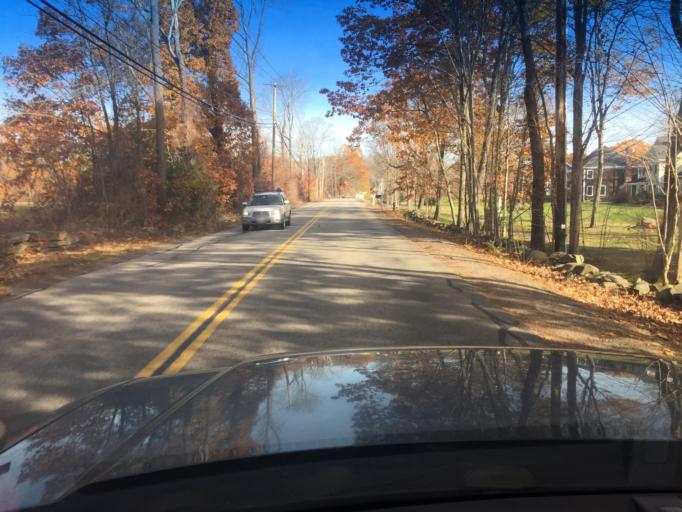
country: US
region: Maine
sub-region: York County
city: York Harbor
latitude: 43.1543
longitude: -70.6359
